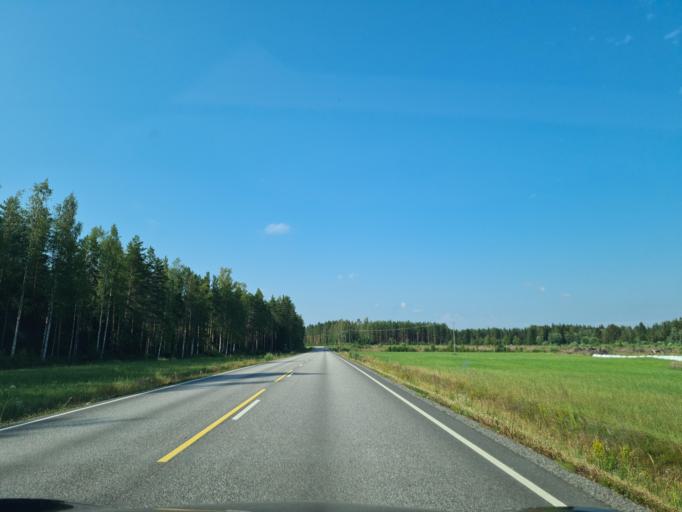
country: FI
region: Satakunta
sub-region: Pohjois-Satakunta
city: Kankaanpaeae
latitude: 61.9536
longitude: 22.5136
